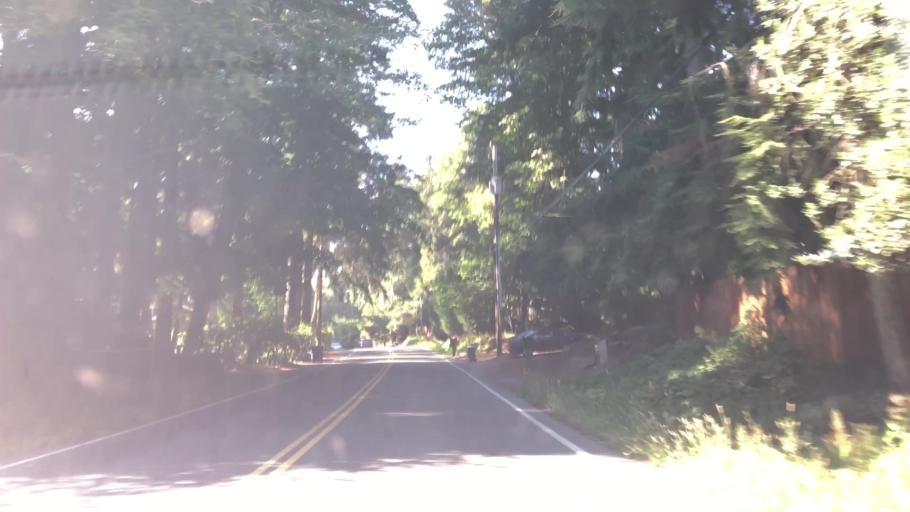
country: US
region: Washington
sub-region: King County
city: Lake Forest Park
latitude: 47.7699
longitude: -122.2854
